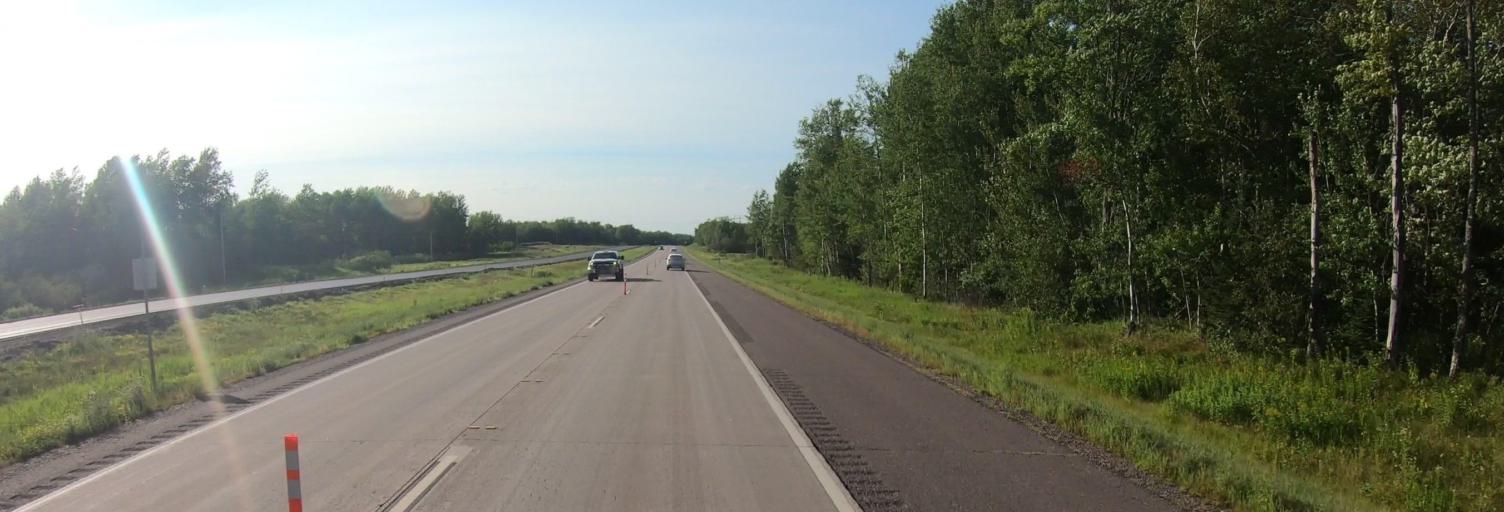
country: US
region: Minnesota
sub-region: Saint Louis County
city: Hermantown
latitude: 46.9115
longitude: -92.3908
